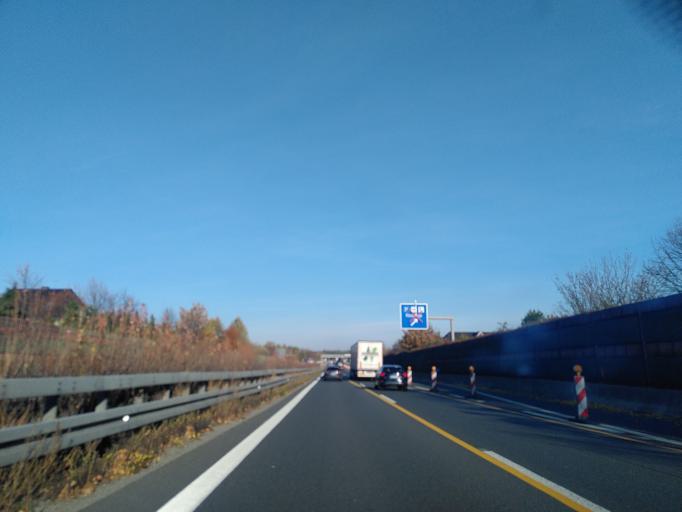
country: DE
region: Saxony
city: Ohorn
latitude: 51.1667
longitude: 14.0545
